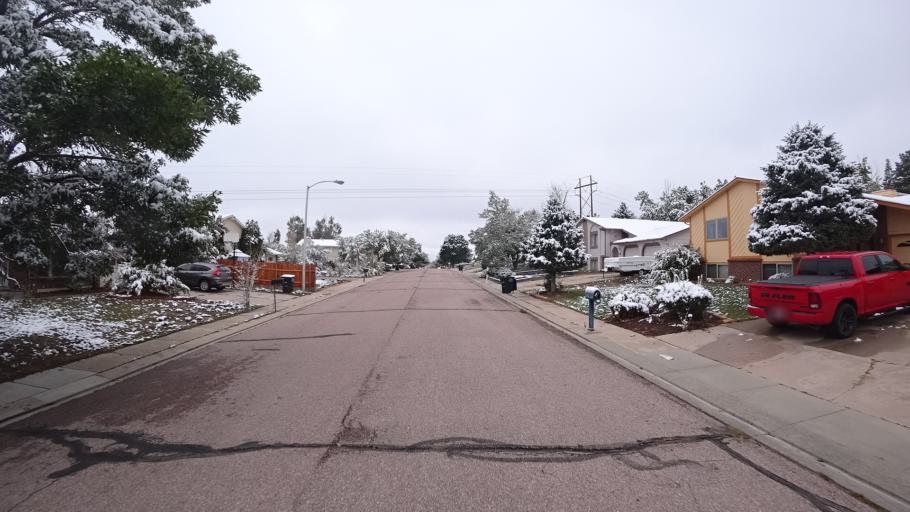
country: US
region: Colorado
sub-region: El Paso County
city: Colorado Springs
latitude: 38.9223
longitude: -104.7854
